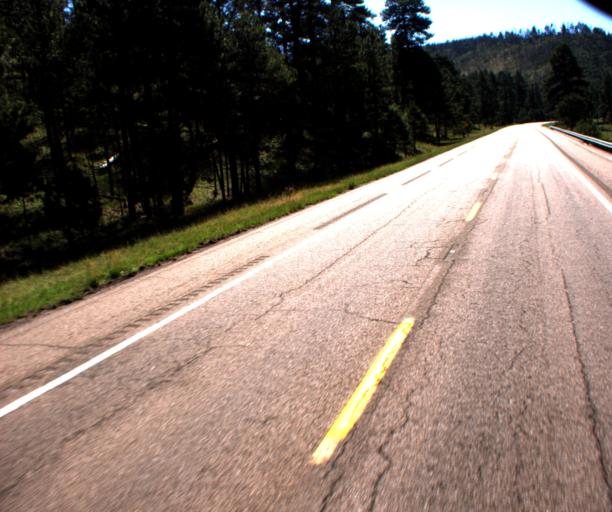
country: US
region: Arizona
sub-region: Apache County
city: Eagar
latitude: 33.9168
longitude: -109.1750
